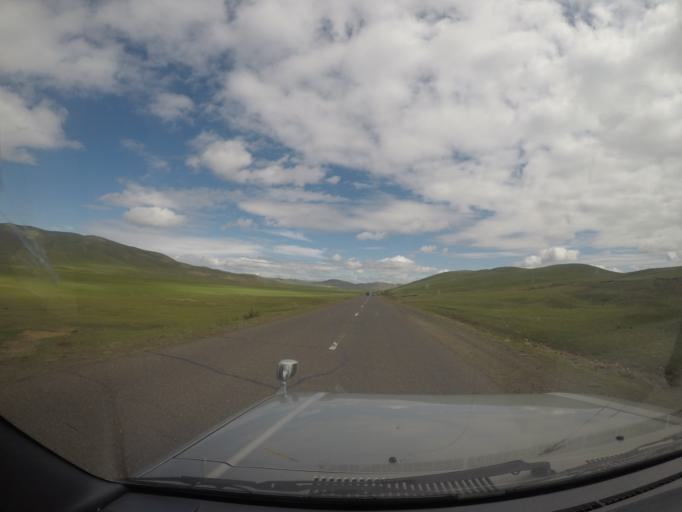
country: MN
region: Hentiy
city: Modot
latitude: 47.7067
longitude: 109.0611
